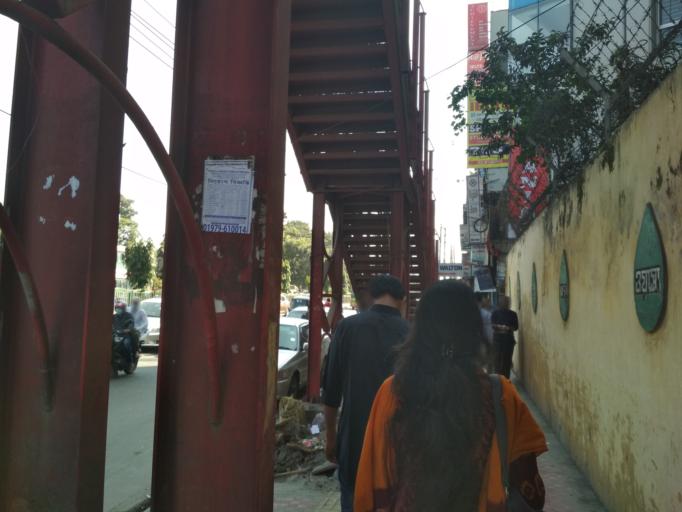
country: BD
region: Dhaka
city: Azimpur
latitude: 23.7596
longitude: 90.3731
